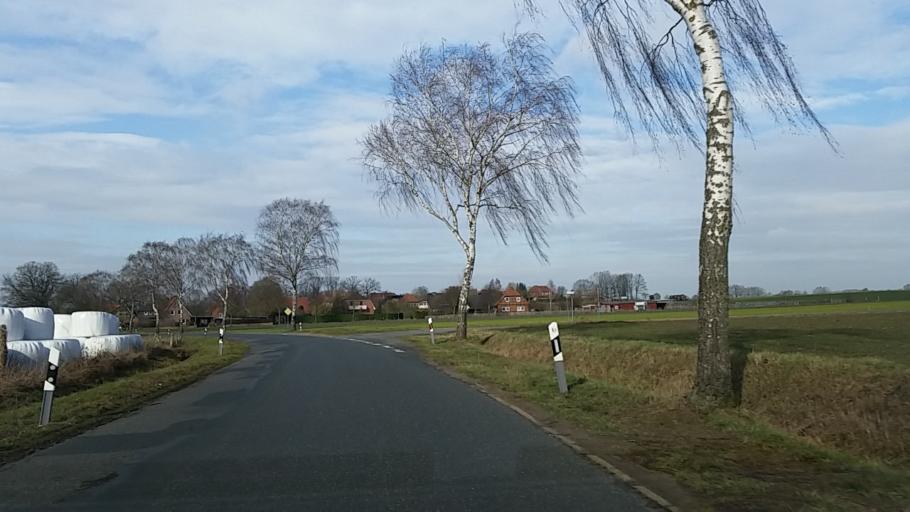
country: DE
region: Lower Saxony
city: Altenmedingen
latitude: 53.1456
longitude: 10.6231
